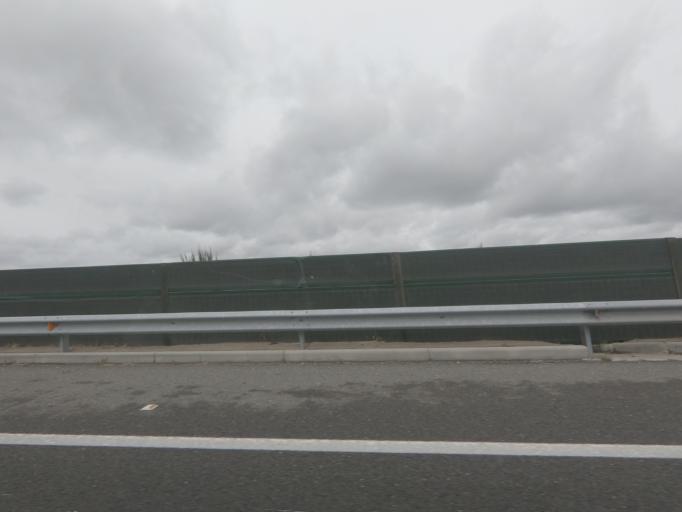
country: ES
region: Castille and Leon
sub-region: Provincia de Salamanca
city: Cantagallo
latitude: 40.3832
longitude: -5.8092
